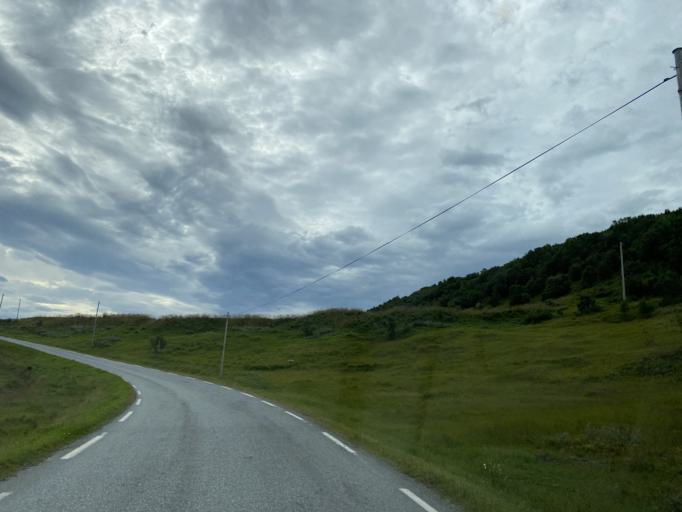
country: NO
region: Troms
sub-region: Karlsoy
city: Hansnes
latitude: 70.0945
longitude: 20.0839
